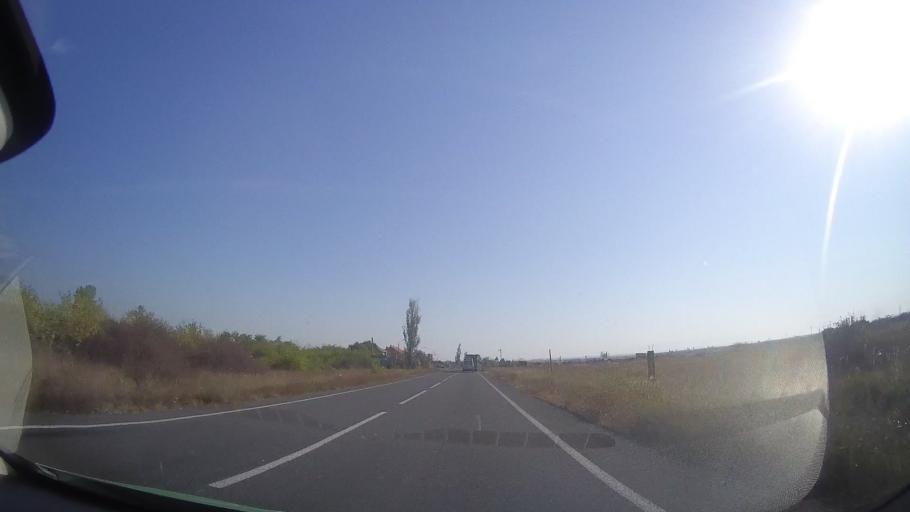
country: RO
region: Timis
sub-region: Comuna Topolovatu Mare
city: Topolovatu Mare
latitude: 45.7776
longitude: 21.6713
